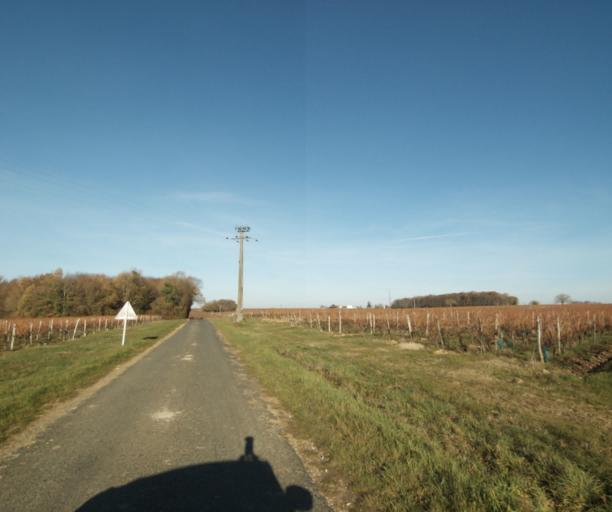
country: FR
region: Poitou-Charentes
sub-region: Departement de la Charente-Maritime
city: Cherac
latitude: 45.7299
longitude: -0.4487
